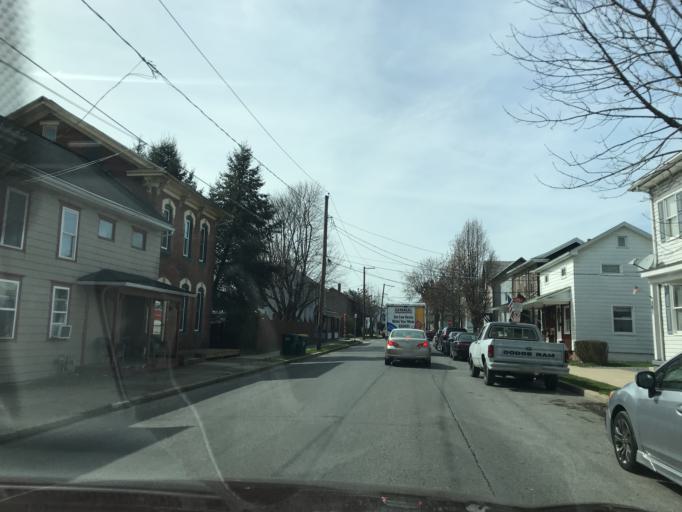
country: US
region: Pennsylvania
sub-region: Northumberland County
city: Northumberland
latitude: 40.8916
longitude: -76.8011
